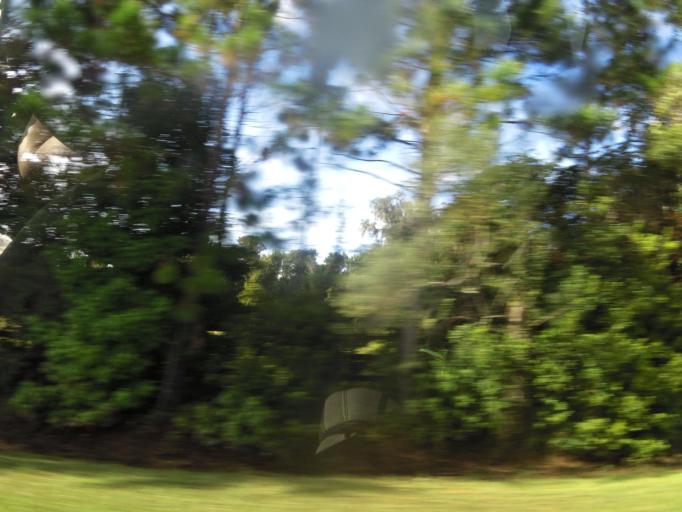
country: US
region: Florida
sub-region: Clay County
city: Green Cove Springs
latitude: 29.9169
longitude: -81.5782
